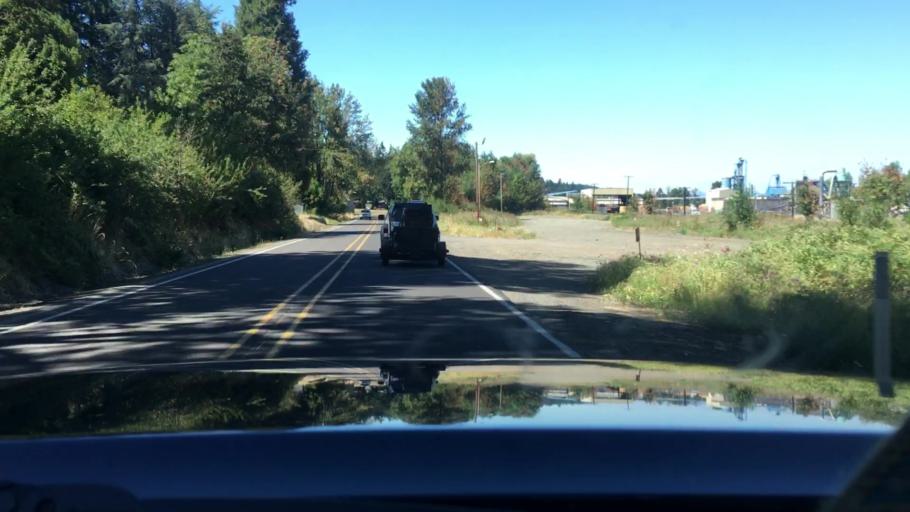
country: US
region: Oregon
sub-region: Lane County
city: Cottage Grove
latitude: 43.8283
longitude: -123.0445
